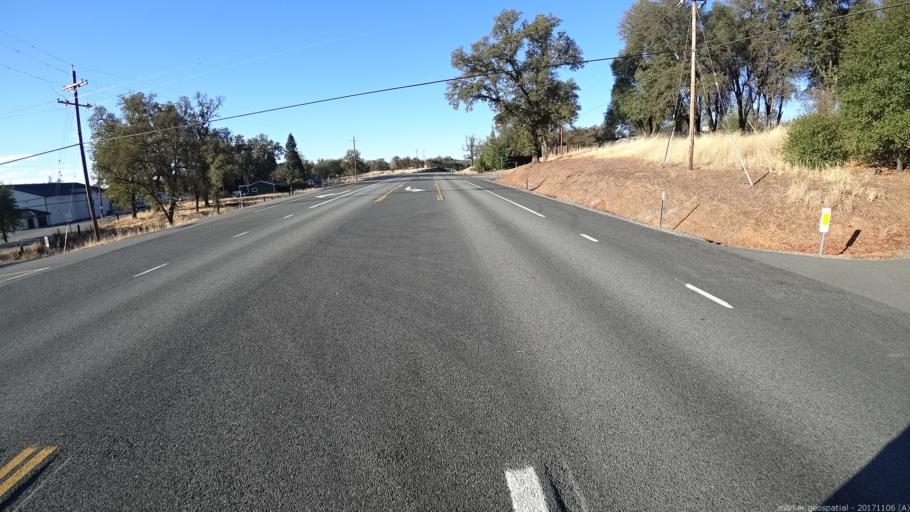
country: US
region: California
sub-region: Shasta County
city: Bella Vista
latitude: 40.6409
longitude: -122.2320
